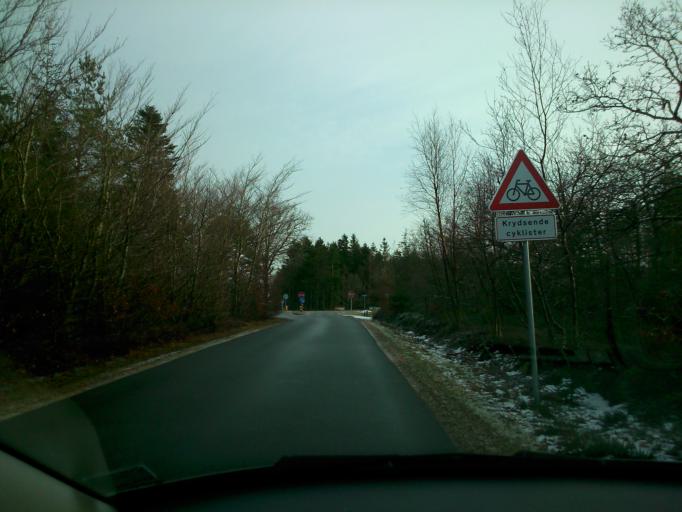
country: DK
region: Central Jutland
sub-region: Ringkobing-Skjern Kommune
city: Skjern
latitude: 55.9990
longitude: 8.4430
